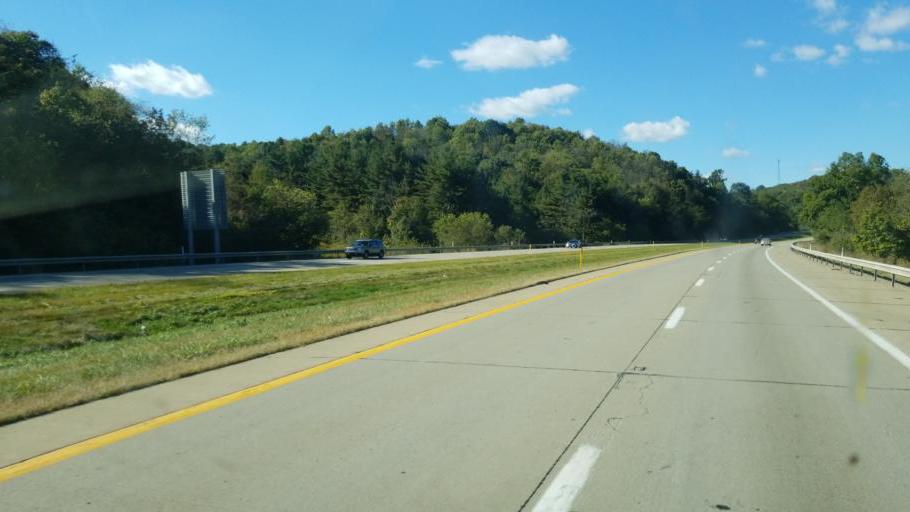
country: US
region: Pennsylvania
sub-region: Greene County
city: Morrisville
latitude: 39.9164
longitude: -80.1616
